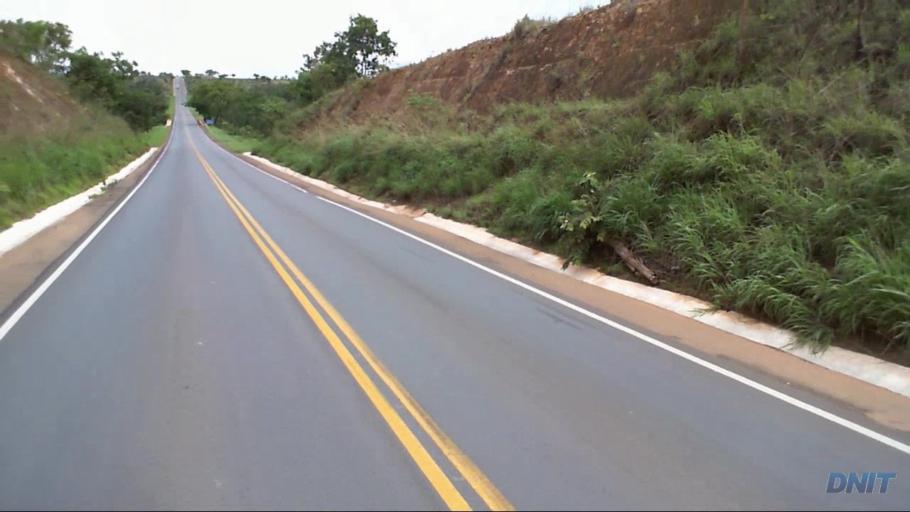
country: BR
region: Goias
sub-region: Padre Bernardo
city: Padre Bernardo
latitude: -15.3540
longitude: -48.2303
